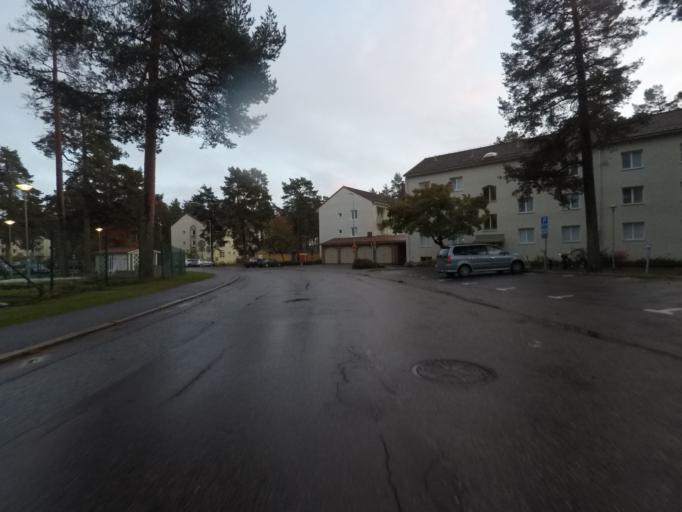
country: SE
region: OErebro
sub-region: Karlskoga Kommun
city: Karlskoga
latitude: 59.3176
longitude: 14.4899
